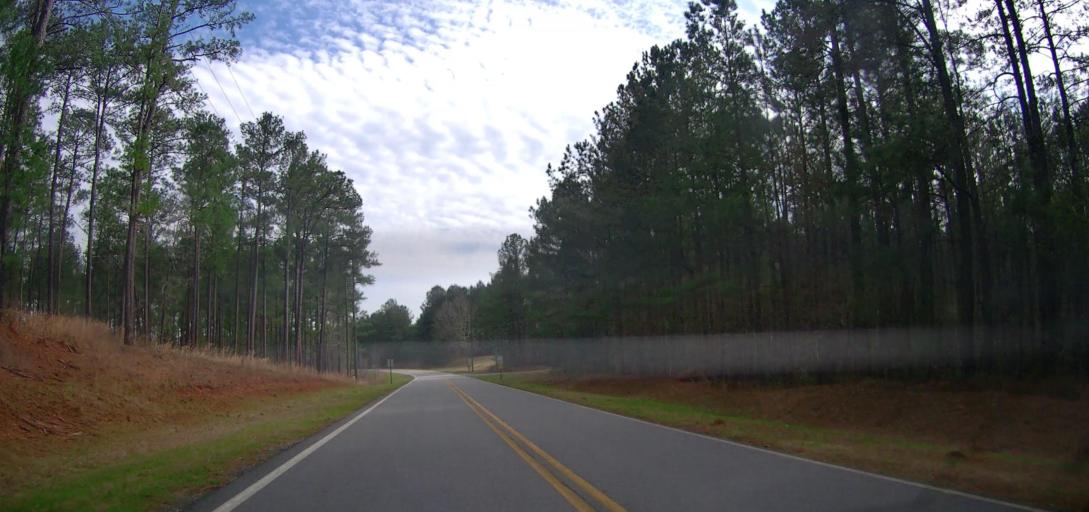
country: US
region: Georgia
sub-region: Jones County
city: Gray
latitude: 33.0663
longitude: -83.7290
